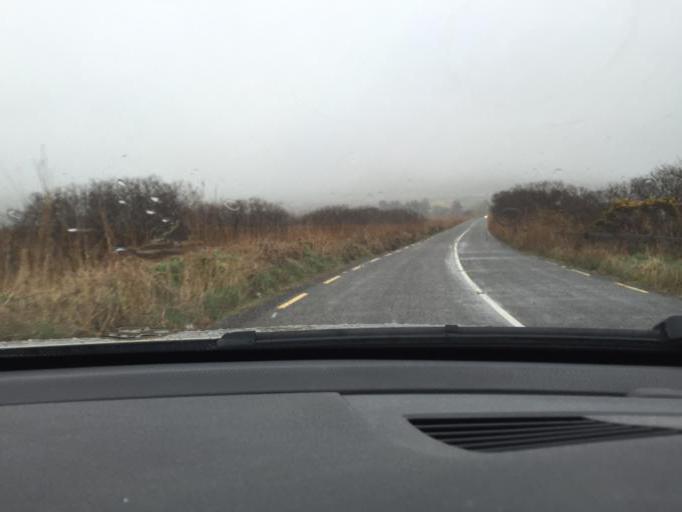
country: IE
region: Munster
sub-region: Ciarrai
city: Dingle
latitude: 52.1336
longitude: -10.3732
